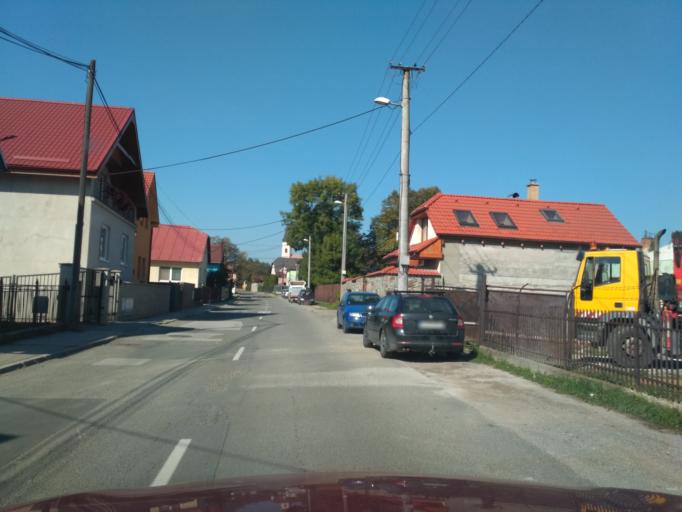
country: SK
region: Kosicky
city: Kosice
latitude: 48.7547
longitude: 21.2564
